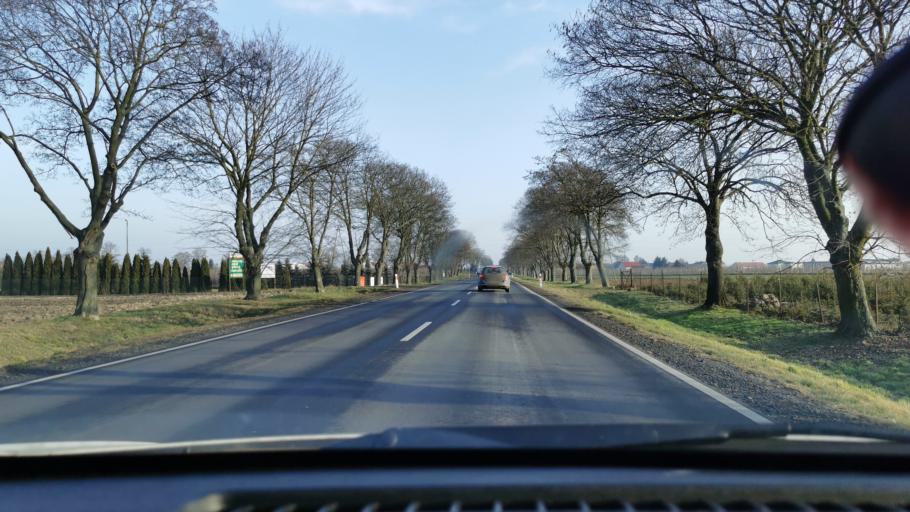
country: PL
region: Lodz Voivodeship
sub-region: Powiat sieradzki
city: Wroblew
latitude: 51.6276
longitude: 18.5604
